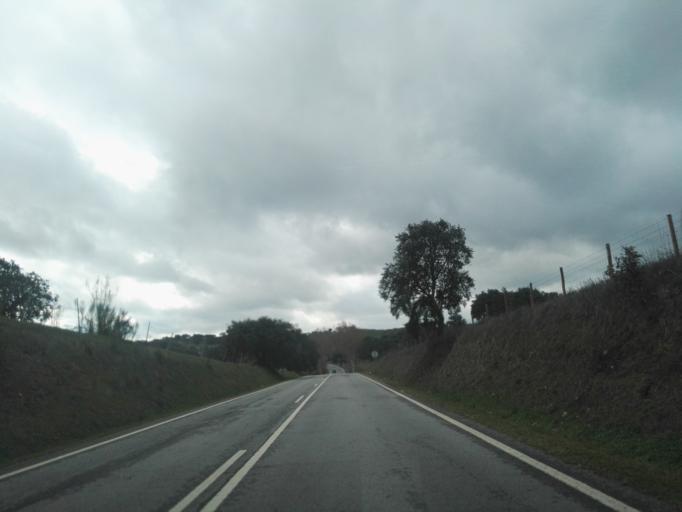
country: PT
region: Portalegre
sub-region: Arronches
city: Arronches
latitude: 39.0942
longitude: -7.2822
